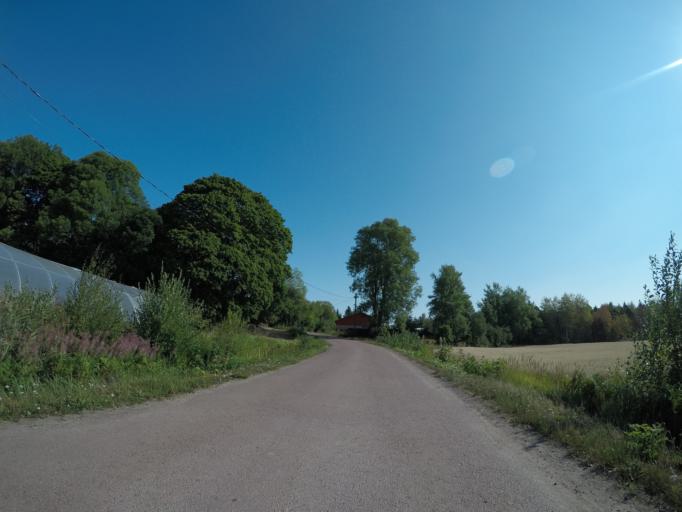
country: AX
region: Alands landsbygd
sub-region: Finstroem
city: Finstroem
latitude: 60.2710
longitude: 19.9396
